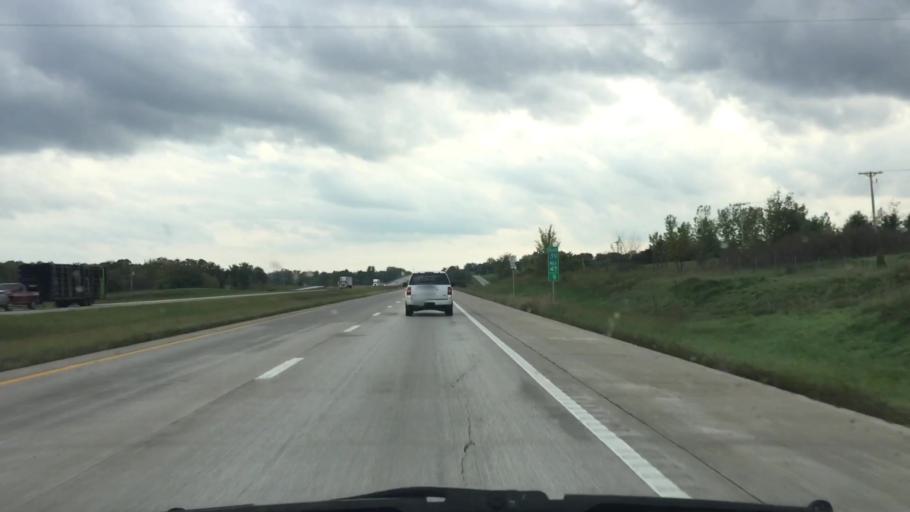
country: US
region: Missouri
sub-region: Clinton County
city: Cameron
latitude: 39.6620
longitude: -94.2374
